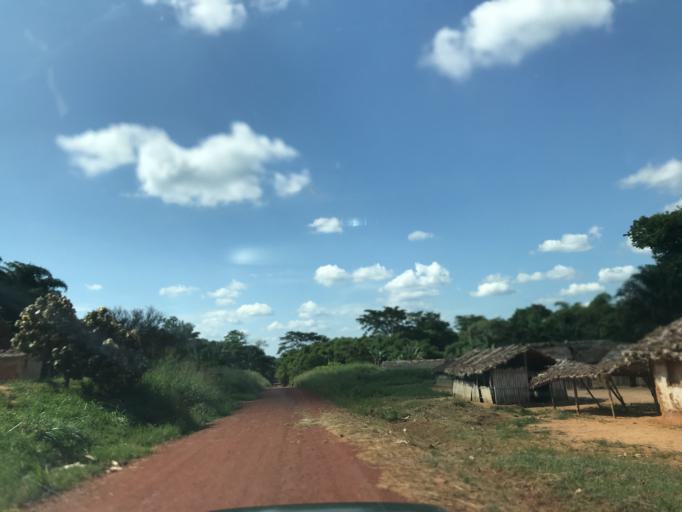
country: CD
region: Eastern Province
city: Kisangani
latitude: 1.2328
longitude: 25.2710
